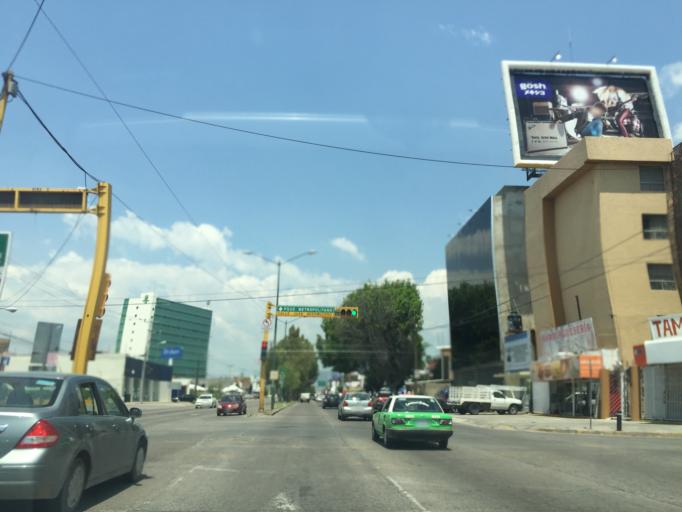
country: MX
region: Guanajuato
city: Leon
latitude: 21.1500
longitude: -101.6848
